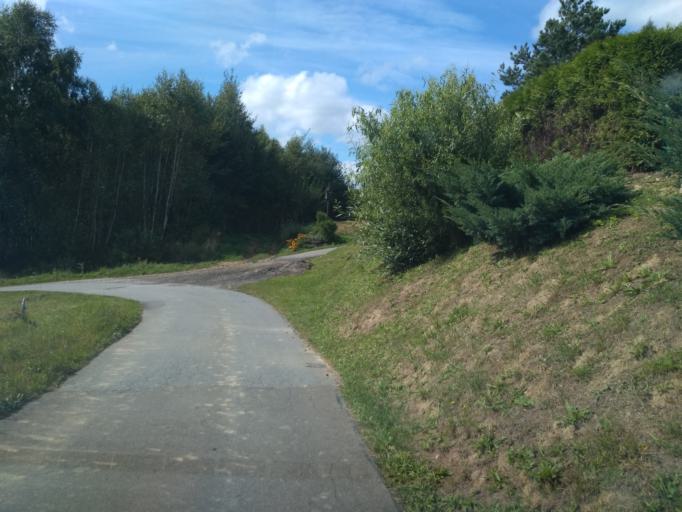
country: PL
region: Subcarpathian Voivodeship
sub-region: Powiat strzyzowski
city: Strzyzow
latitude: 49.8505
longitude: 21.8251
